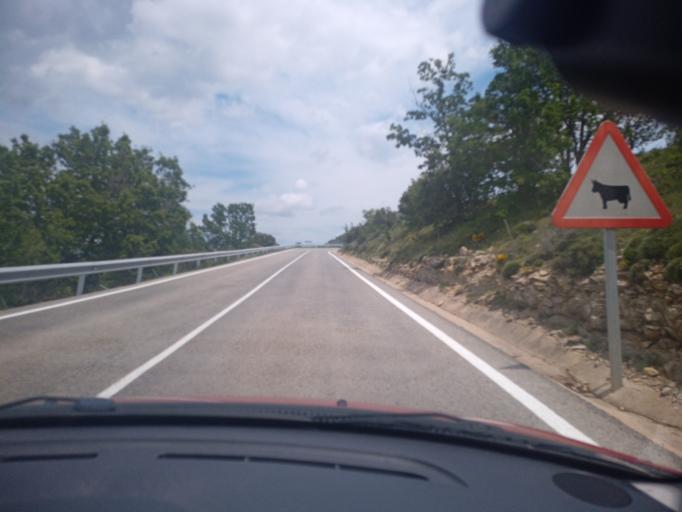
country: ES
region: Valencia
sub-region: Provincia de Castello
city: Ares del Maestre
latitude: 40.4610
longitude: -0.1521
